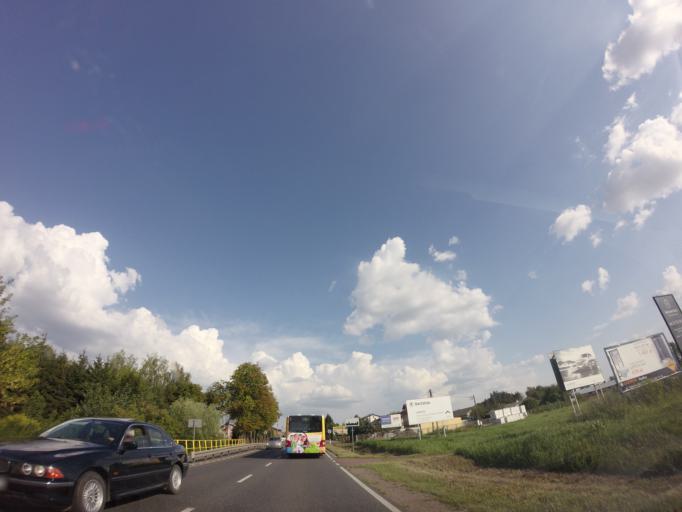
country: PL
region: Masovian Voivodeship
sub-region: Powiat siedlecki
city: Suchozebry
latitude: 52.2060
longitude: 22.2428
